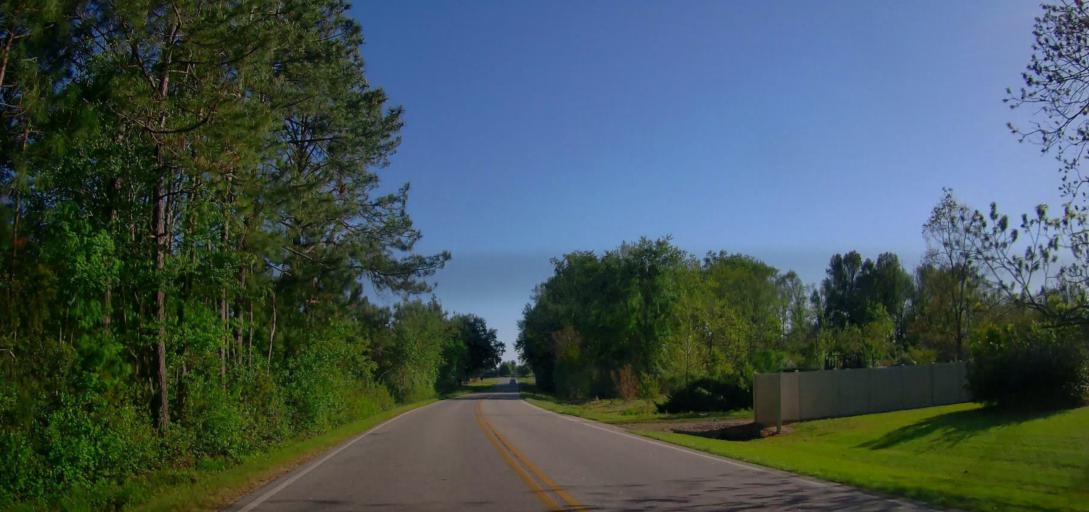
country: US
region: Georgia
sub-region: Ben Hill County
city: Fitzgerald
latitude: 31.7390
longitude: -83.2347
